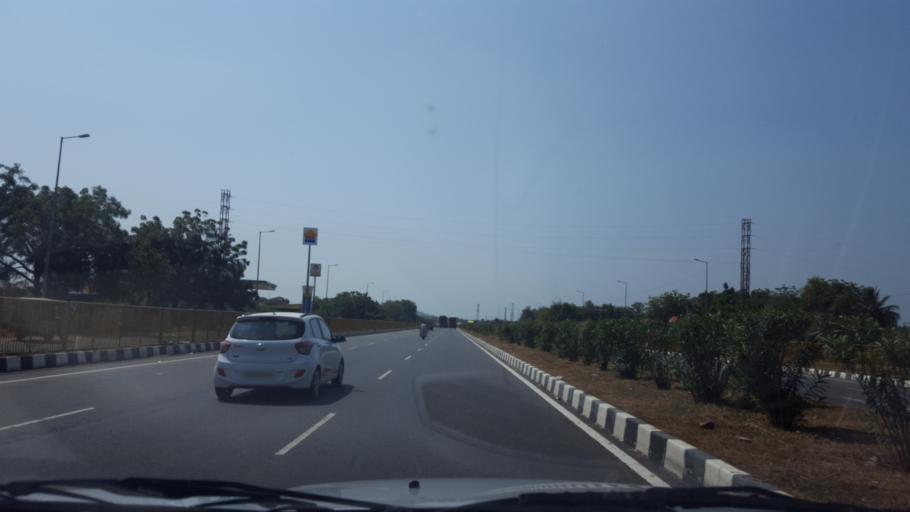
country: IN
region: Andhra Pradesh
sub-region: Prakasam
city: pedda nakkalapalem
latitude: 15.9520
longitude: 80.0869
